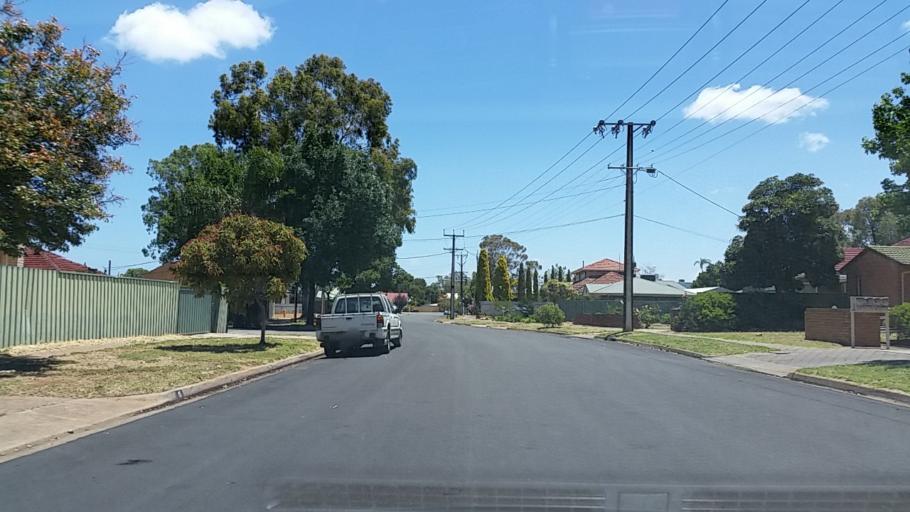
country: AU
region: South Australia
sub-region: Salisbury
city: Salisbury
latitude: -34.7662
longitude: 138.6409
